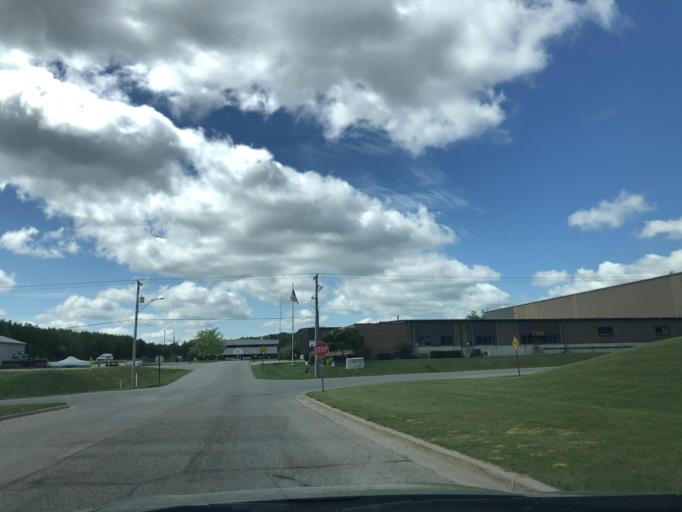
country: US
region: Michigan
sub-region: Clare County
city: Harrison
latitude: 44.0173
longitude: -84.8118
